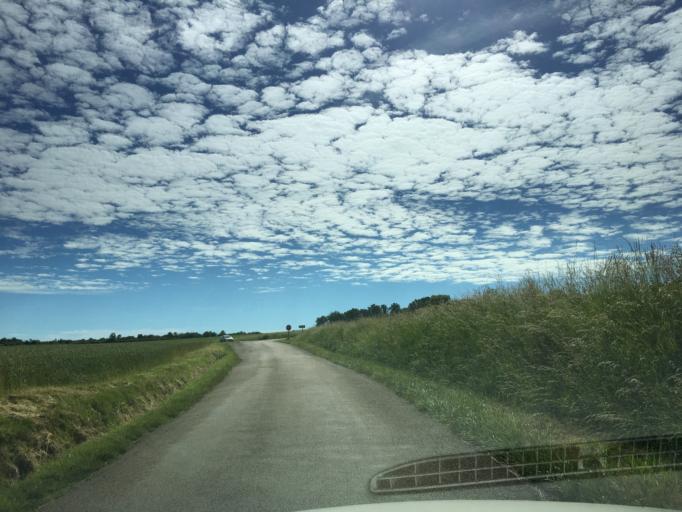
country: FR
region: Bourgogne
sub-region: Departement de l'Yonne
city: Saint-Georges-sur-Baulche
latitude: 47.7651
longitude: 3.5188
